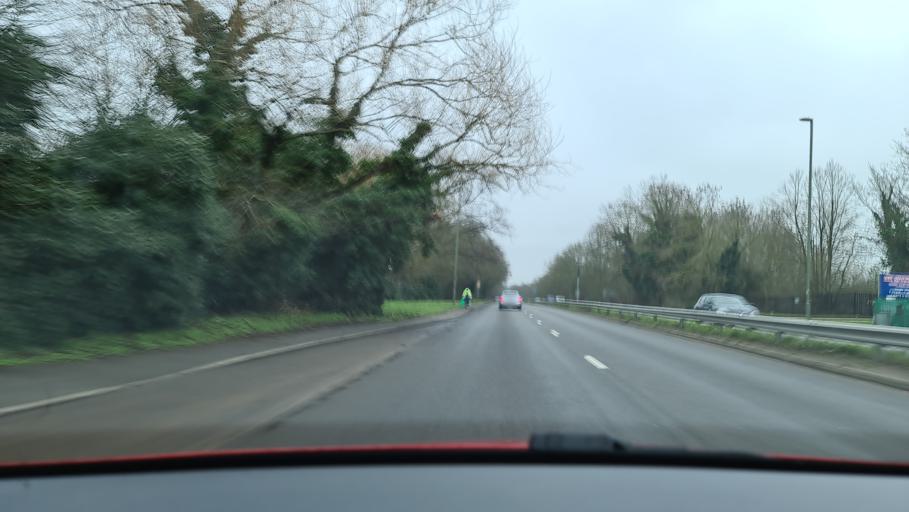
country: GB
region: England
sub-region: Surrey
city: Staines
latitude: 51.4262
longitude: -0.4703
